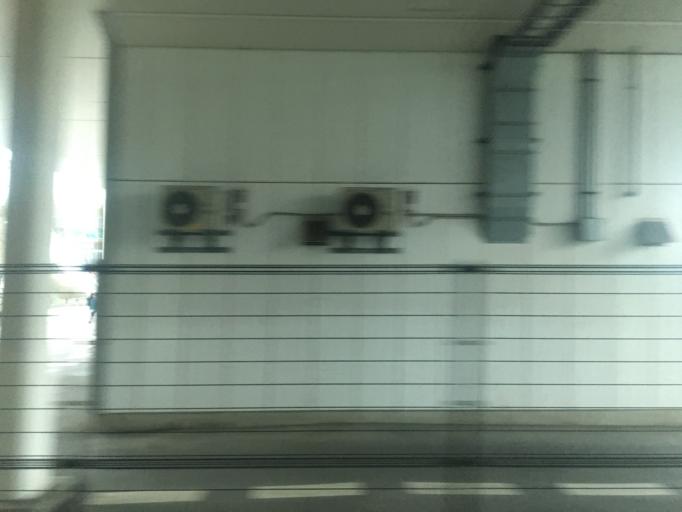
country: JP
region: Saitama
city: Ageoshimo
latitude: 35.9732
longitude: 139.5883
